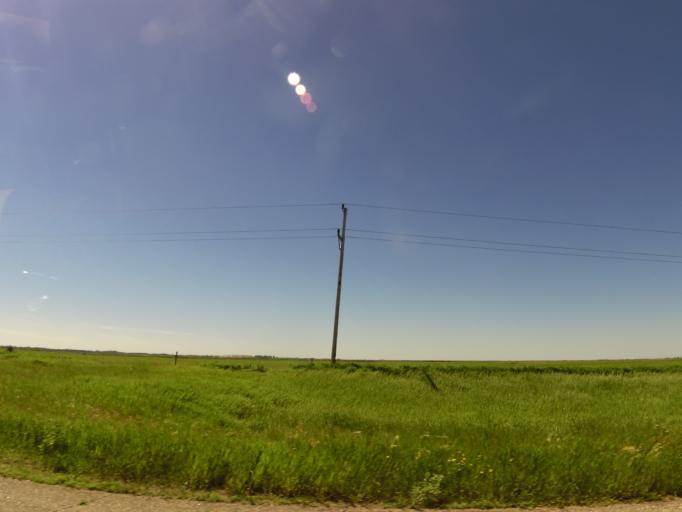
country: US
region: Minnesota
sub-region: Red Lake County
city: Red Lake Falls
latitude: 47.7601
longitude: -96.3103
